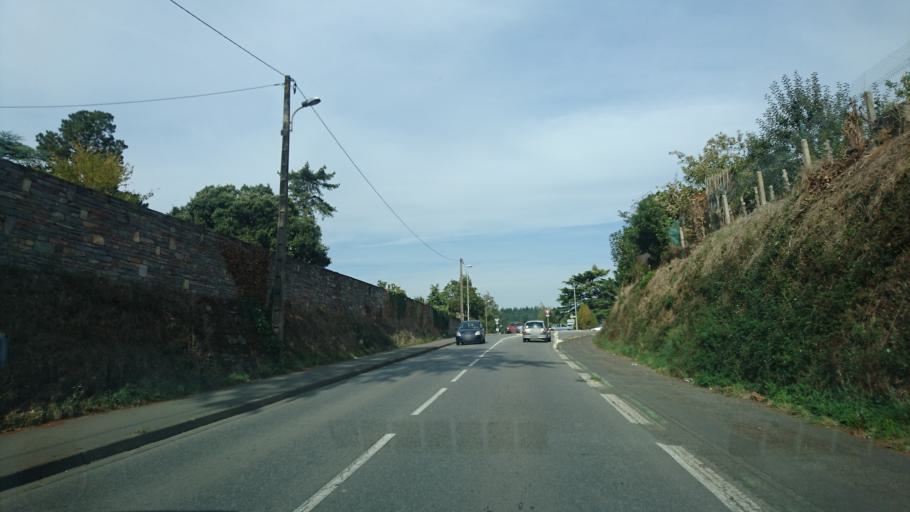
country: FR
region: Brittany
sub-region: Departement d'Ille-et-Vilaine
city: Redon
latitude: 47.6568
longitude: -2.0841
